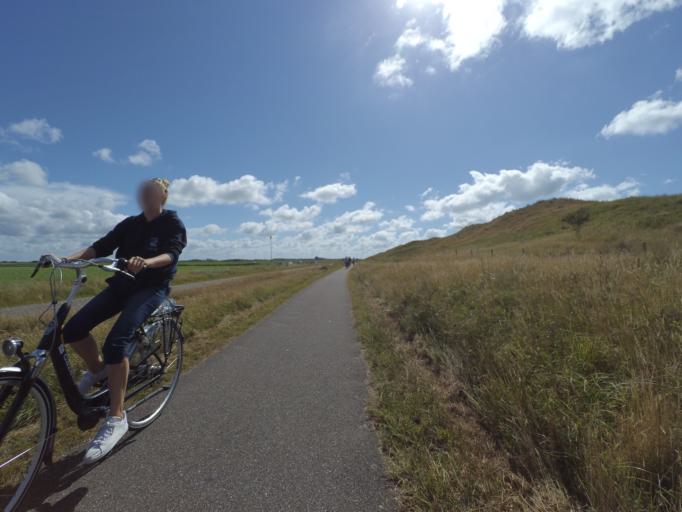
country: NL
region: North Holland
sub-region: Gemeente Texel
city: Den Burg
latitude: 53.1209
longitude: 4.8050
